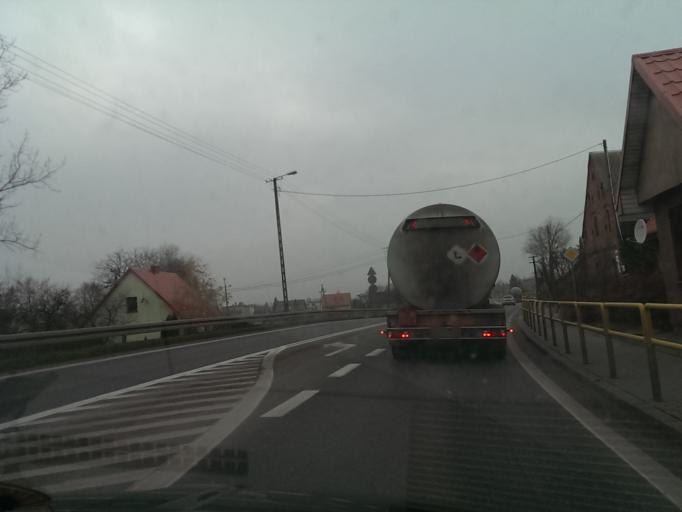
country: PL
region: Kujawsko-Pomorskie
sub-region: Powiat nakielski
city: Slesin
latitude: 53.1652
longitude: 17.7008
